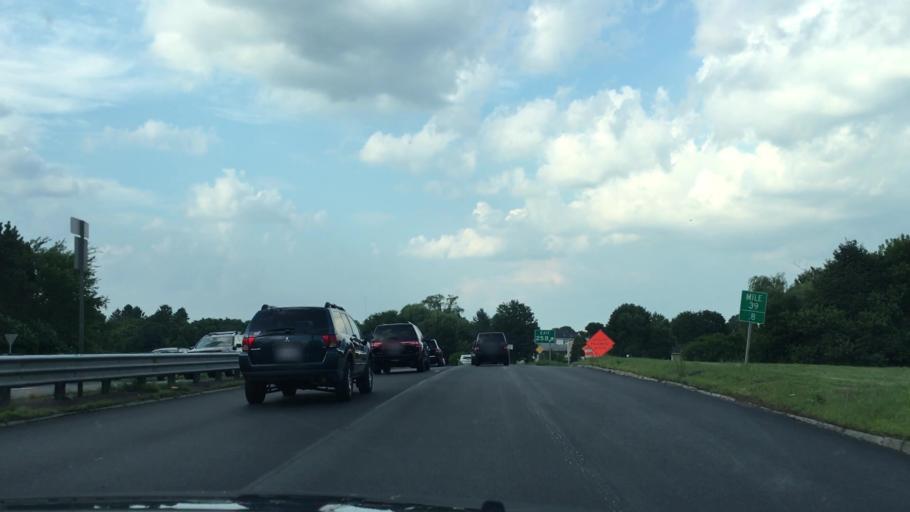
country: US
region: Massachusetts
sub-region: Essex County
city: Peabody
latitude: 42.5404
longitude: -70.9374
